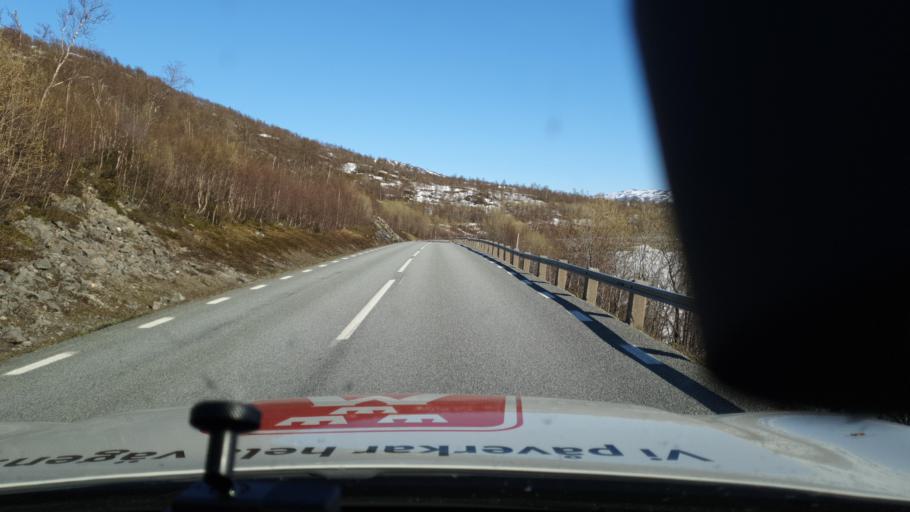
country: NO
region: Nordland
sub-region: Rana
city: Mo i Rana
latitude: 66.1096
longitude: 14.8164
